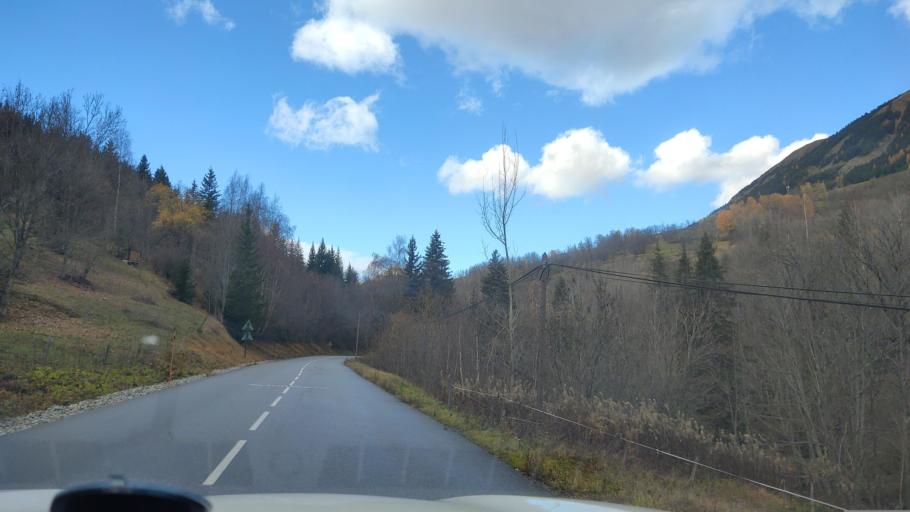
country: FR
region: Rhone-Alpes
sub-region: Departement de la Savoie
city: Saint-Jean-de-Maurienne
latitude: 45.1928
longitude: 6.2855
